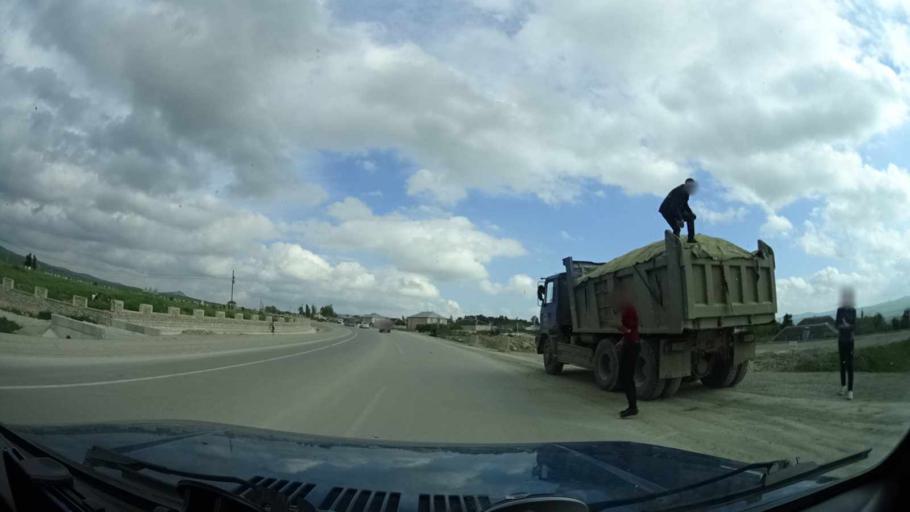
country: AZ
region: Samaxi
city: Shamakhi
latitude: 40.5927
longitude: 48.7035
